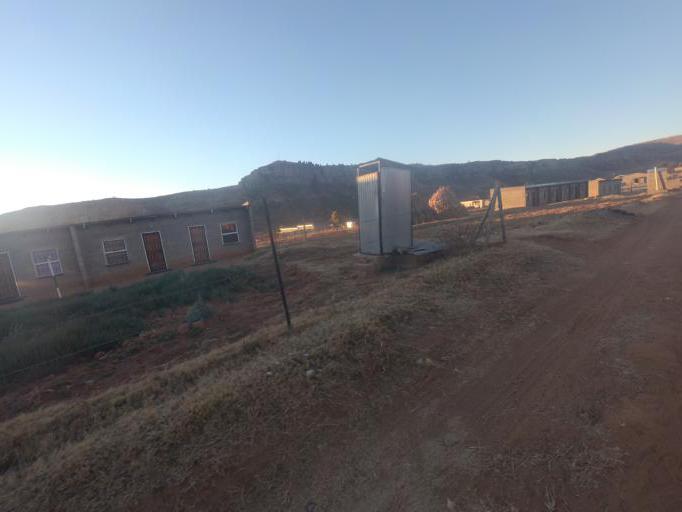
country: LS
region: Maseru
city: Nako
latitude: -29.4404
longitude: 27.7105
